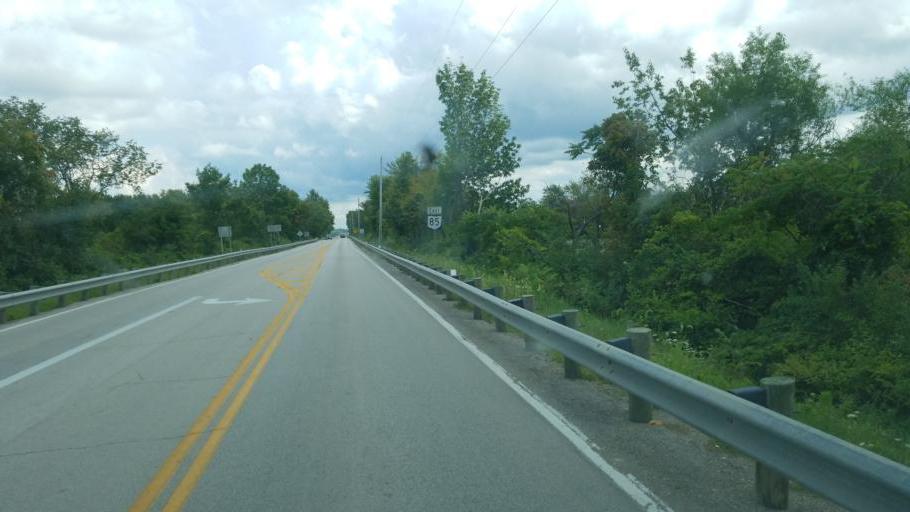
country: US
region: Ohio
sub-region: Ashtabula County
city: Andover
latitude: 41.6072
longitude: -80.5413
